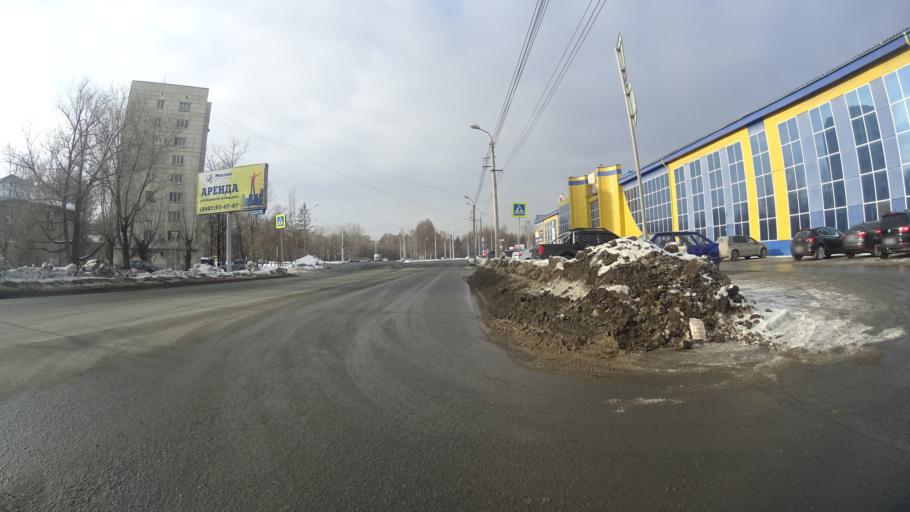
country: RU
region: Chelyabinsk
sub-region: Gorod Chelyabinsk
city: Chelyabinsk
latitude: 55.1263
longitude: 61.3683
